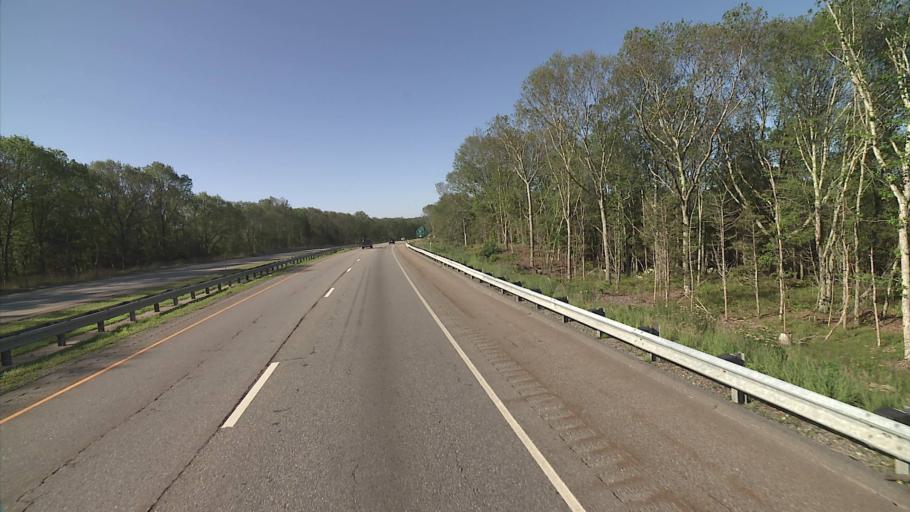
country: US
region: Connecticut
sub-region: Windham County
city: Plainfield Village
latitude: 41.6353
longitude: -71.9370
